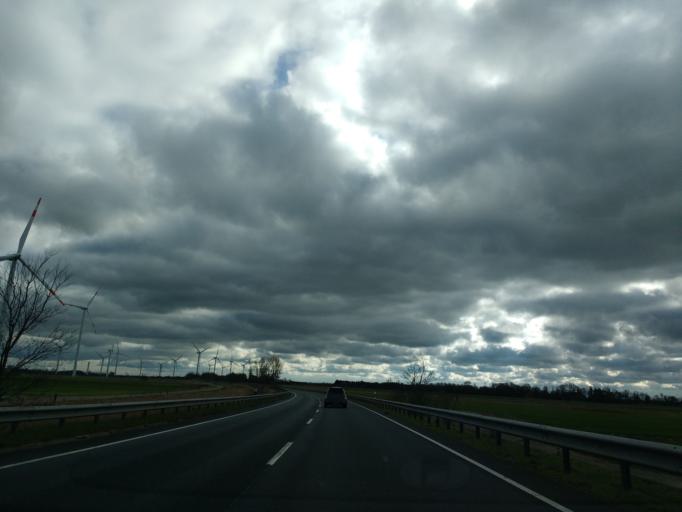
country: DE
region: Lower Saxony
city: Cuxhaven
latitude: 53.8223
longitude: 8.6885
